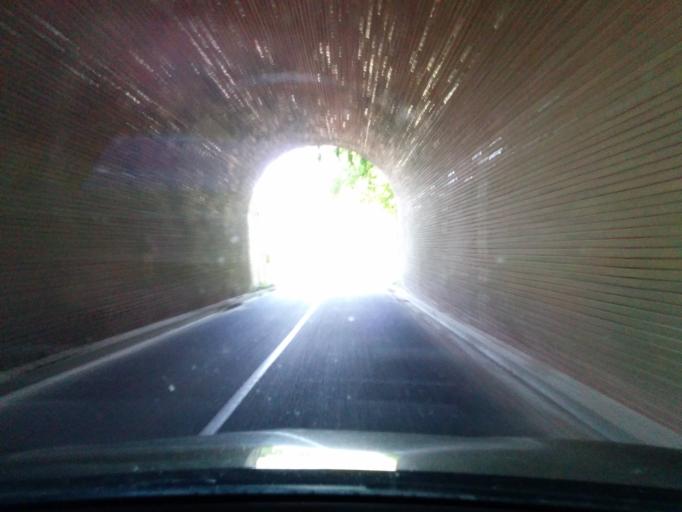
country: FR
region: Haute-Normandie
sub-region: Departement de l'Eure
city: Charleval
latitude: 49.3482
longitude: 1.4546
